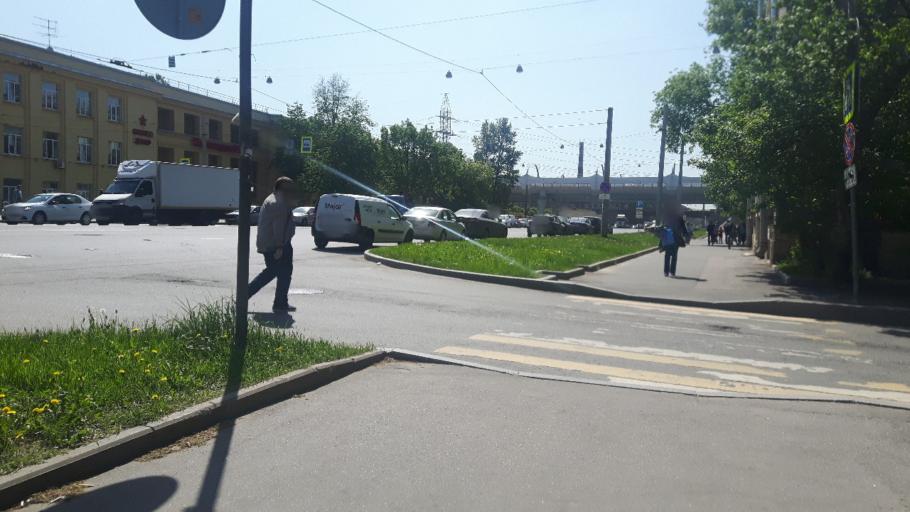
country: RU
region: St.-Petersburg
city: Avtovo
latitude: 59.8858
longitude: 30.2737
